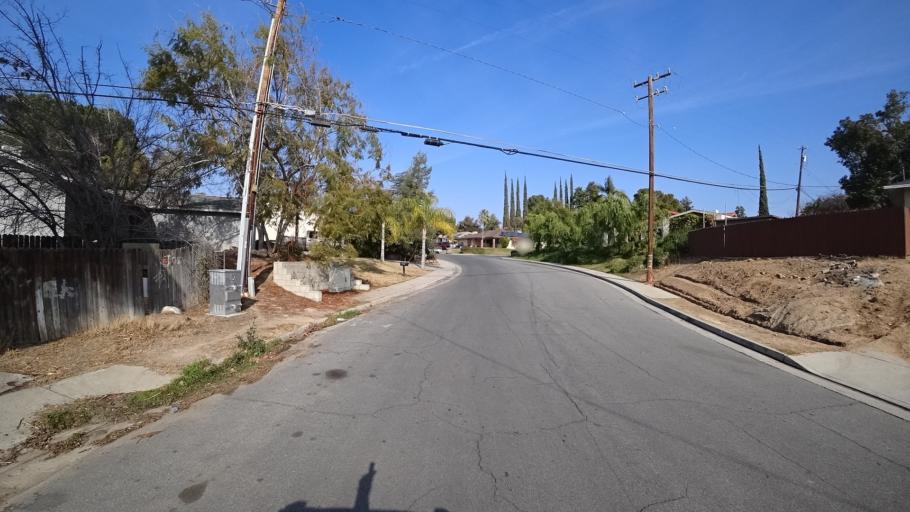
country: US
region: California
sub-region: Kern County
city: Bakersfield
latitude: 35.3866
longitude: -118.9627
